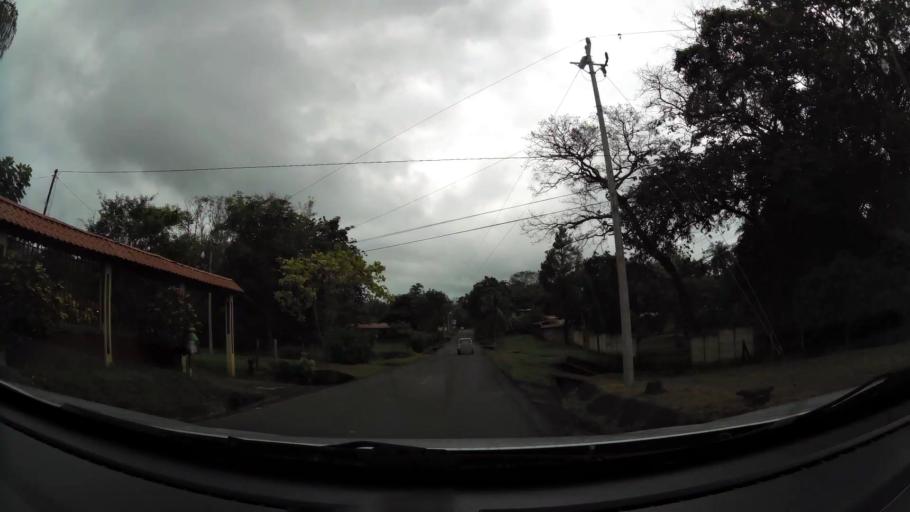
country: CR
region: Puntarenas
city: Esparza
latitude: 9.9951
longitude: -84.6550
